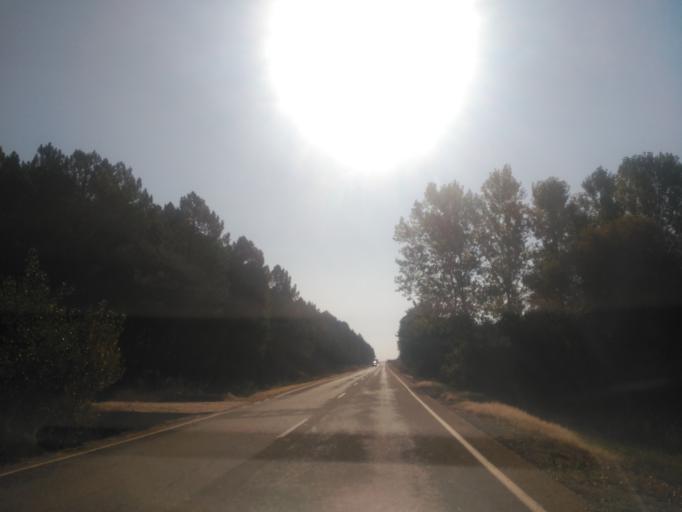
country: ES
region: Castille and Leon
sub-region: Provincia de Soria
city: San Leonardo de Yague
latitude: 41.8094
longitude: -3.0570
